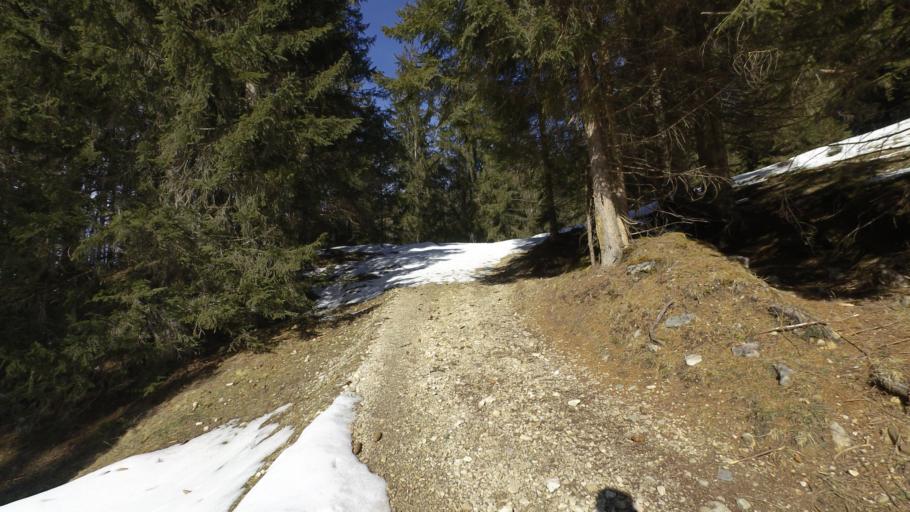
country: DE
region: Bavaria
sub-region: Upper Bavaria
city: Reit im Winkl
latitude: 47.6883
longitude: 12.4447
